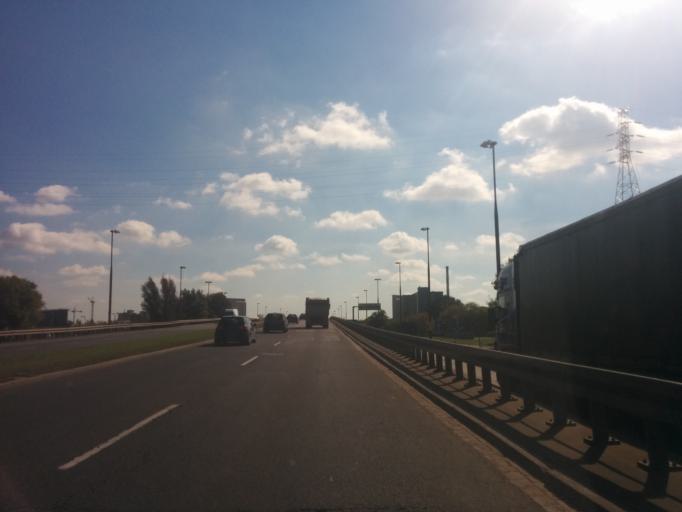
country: PL
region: Masovian Voivodeship
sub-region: Warszawa
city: Bialoleka
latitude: 52.3094
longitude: 20.9814
